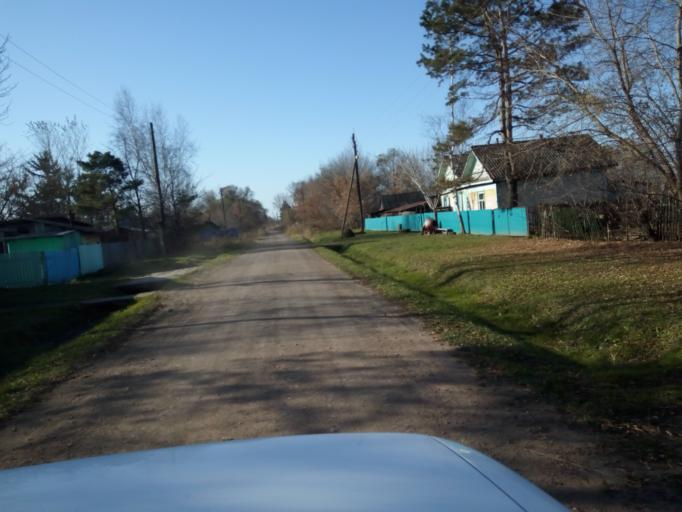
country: RU
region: Primorskiy
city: Lazo
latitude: 45.8701
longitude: 133.6434
